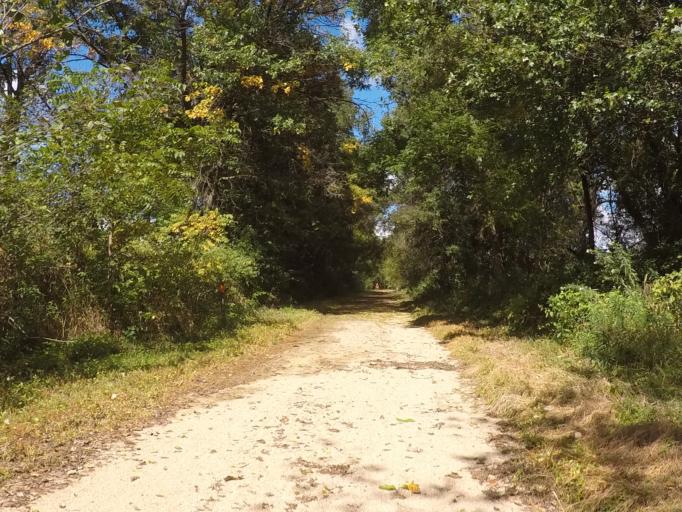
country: US
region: Wisconsin
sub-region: Richland County
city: Richland Center
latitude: 43.2891
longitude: -90.3240
